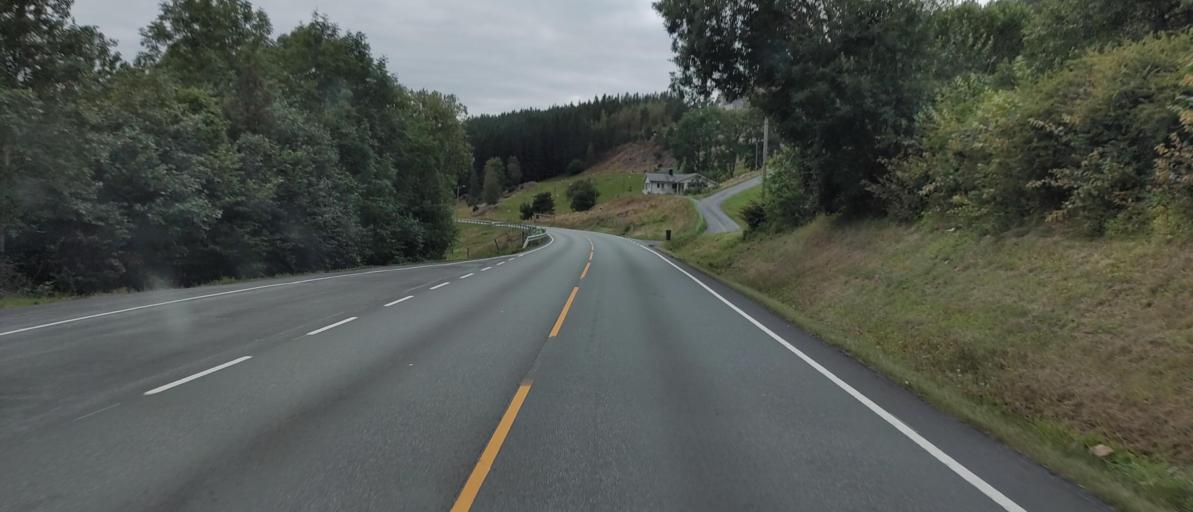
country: NO
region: More og Romsdal
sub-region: Rauma
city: Andalsnes
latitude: 62.5805
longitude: 7.5586
